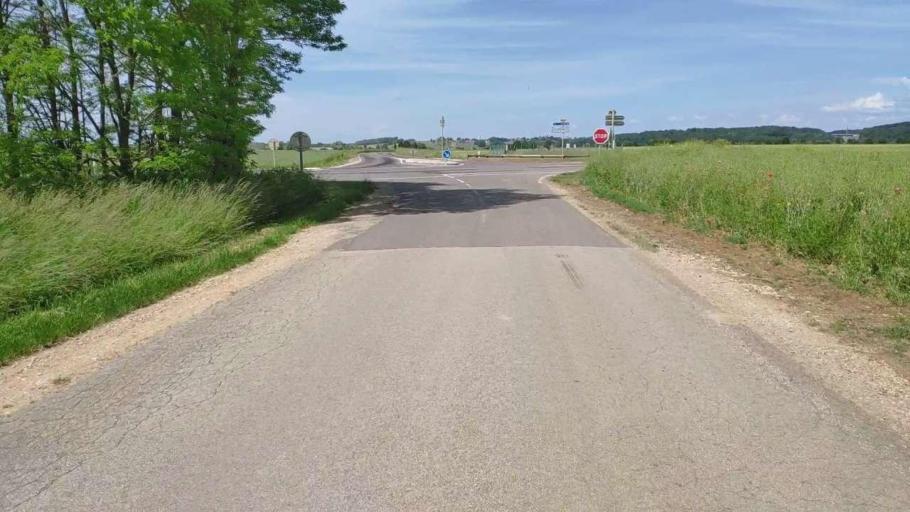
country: FR
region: Franche-Comte
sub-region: Departement du Jura
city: Bletterans
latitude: 46.7554
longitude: 5.4963
